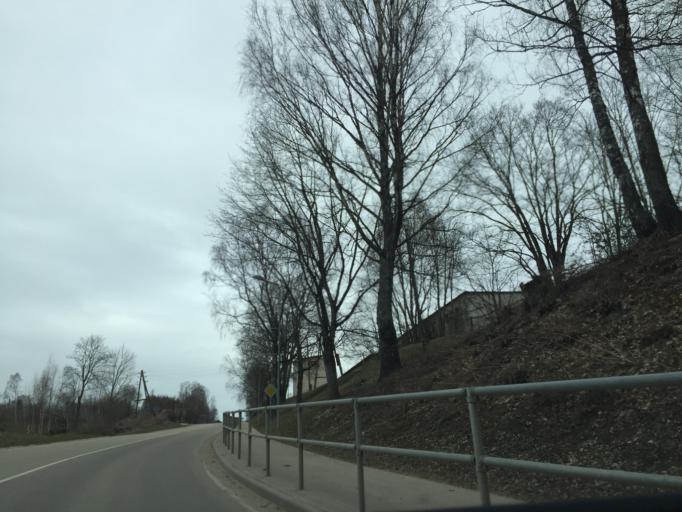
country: LV
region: Kraslavas Rajons
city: Kraslava
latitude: 55.9025
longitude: 27.1545
